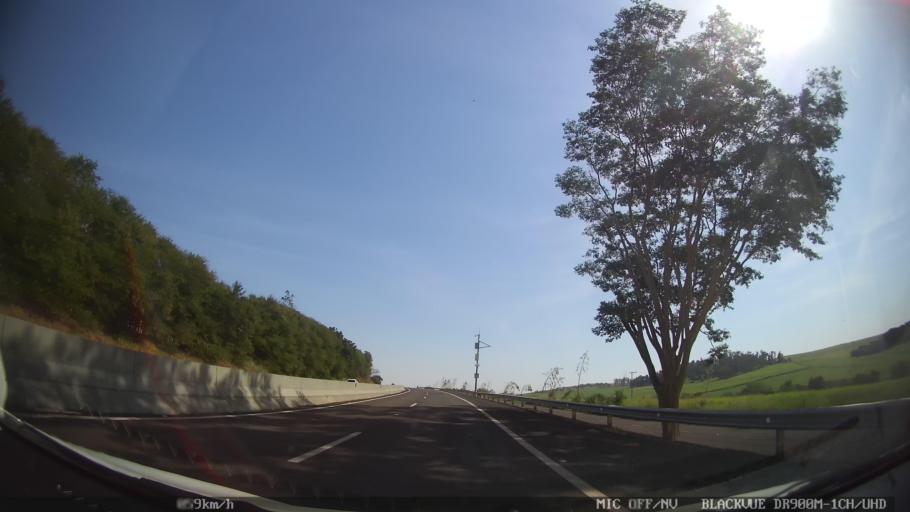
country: BR
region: Sao Paulo
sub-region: Ribeirao Preto
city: Ribeirao Preto
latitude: -21.1681
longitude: -47.8683
